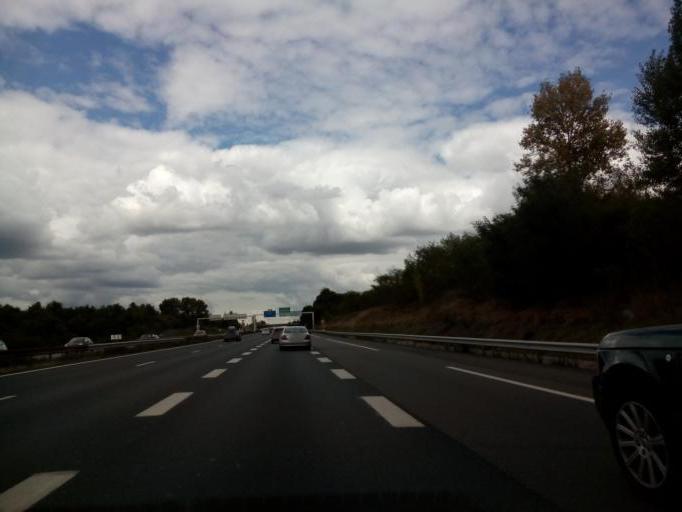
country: FR
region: Rhone-Alpes
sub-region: Departement du Rhone
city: Dardilly
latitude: 45.8141
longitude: 4.7667
